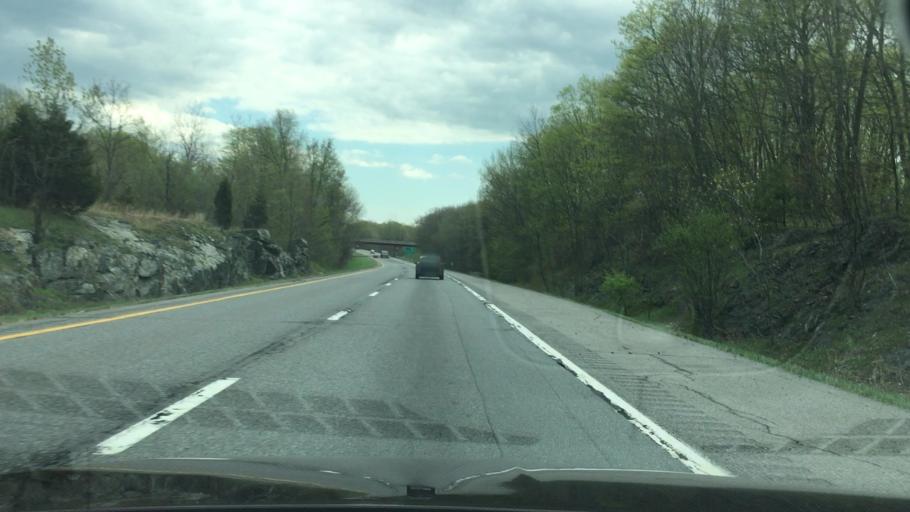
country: US
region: New York
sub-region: Putnam County
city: Lake Carmel
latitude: 41.5233
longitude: -73.6934
